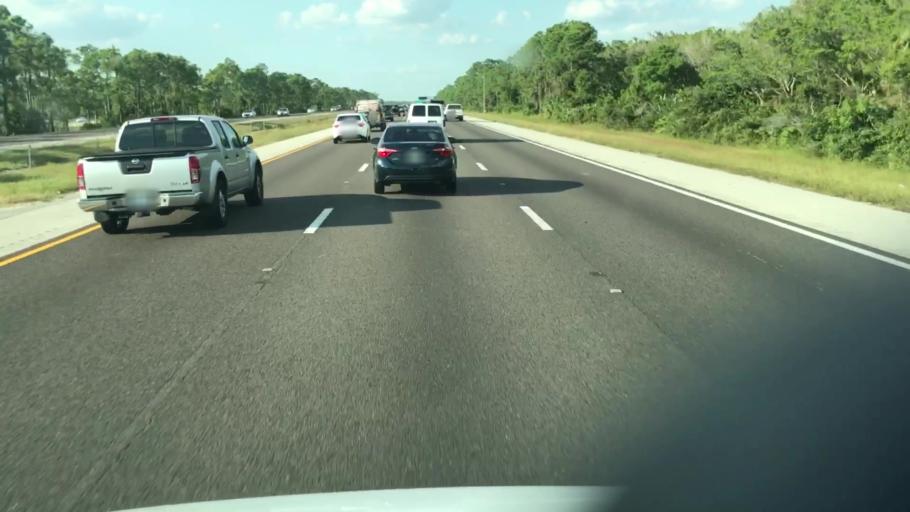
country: US
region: Florida
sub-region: Lee County
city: Three Oaks
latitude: 26.4602
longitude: -81.7869
